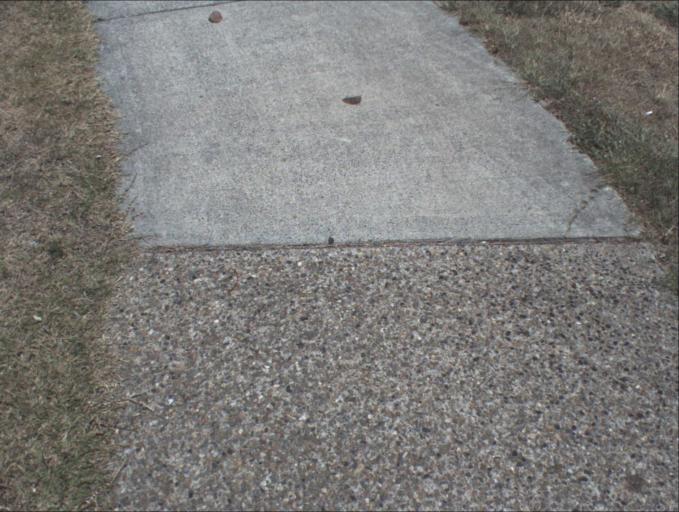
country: AU
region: Queensland
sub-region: Logan
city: Beenleigh
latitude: -27.7059
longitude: 153.2084
